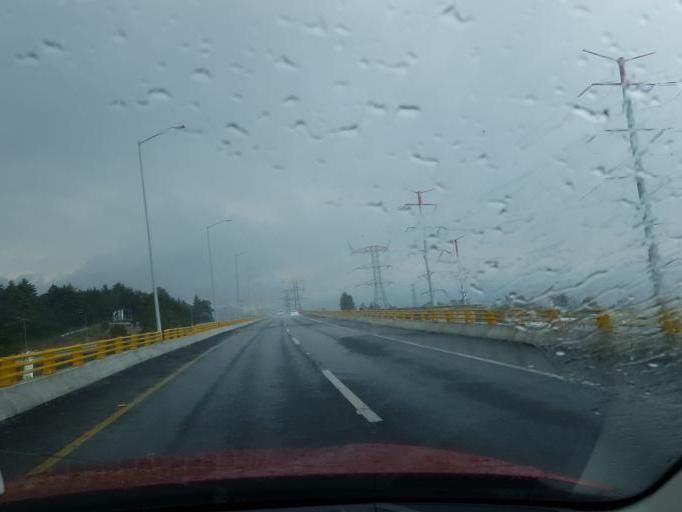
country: MX
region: Mexico
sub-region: Ocoyoacac
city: San Antonio el Llanito
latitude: 19.2822
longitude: -99.4871
